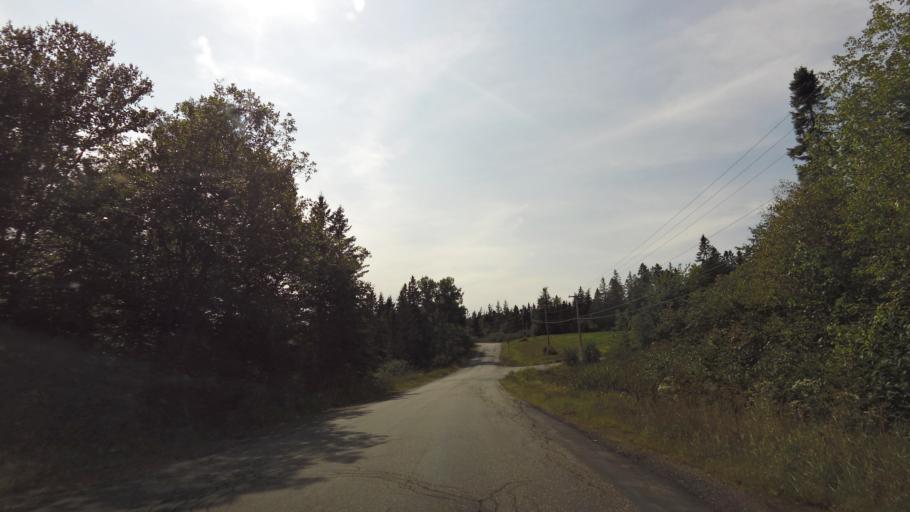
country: CA
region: New Brunswick
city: Hampton
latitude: 45.5696
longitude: -65.9062
